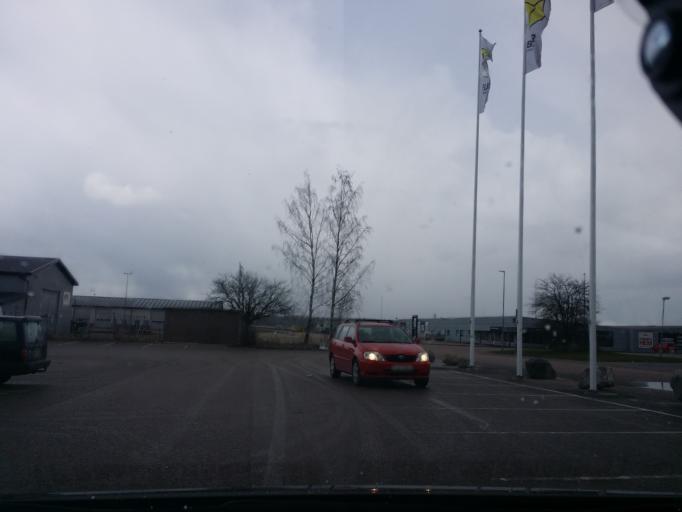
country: SE
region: Vaestmanland
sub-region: Sala Kommun
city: Sala
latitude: 59.9172
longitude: 16.6258
